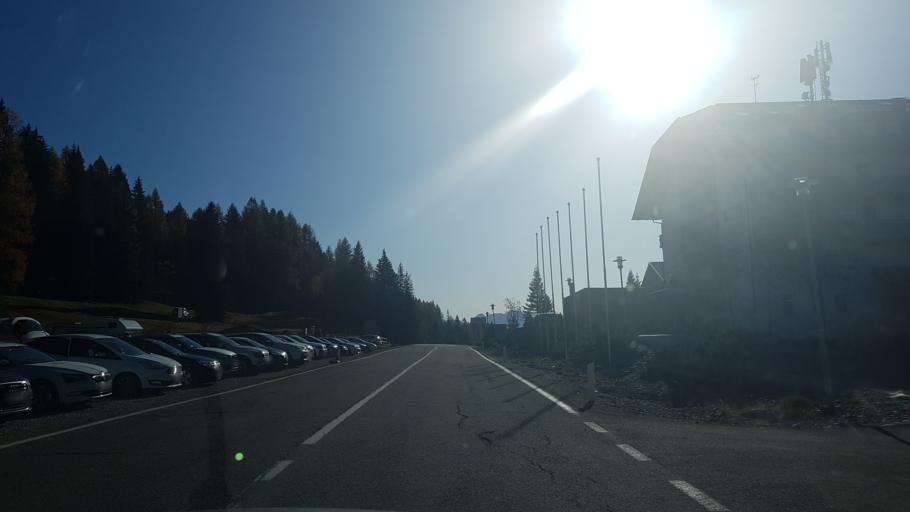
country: IT
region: Trentino-Alto Adige
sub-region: Bolzano
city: Sesto
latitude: 46.6564
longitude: 12.4194
